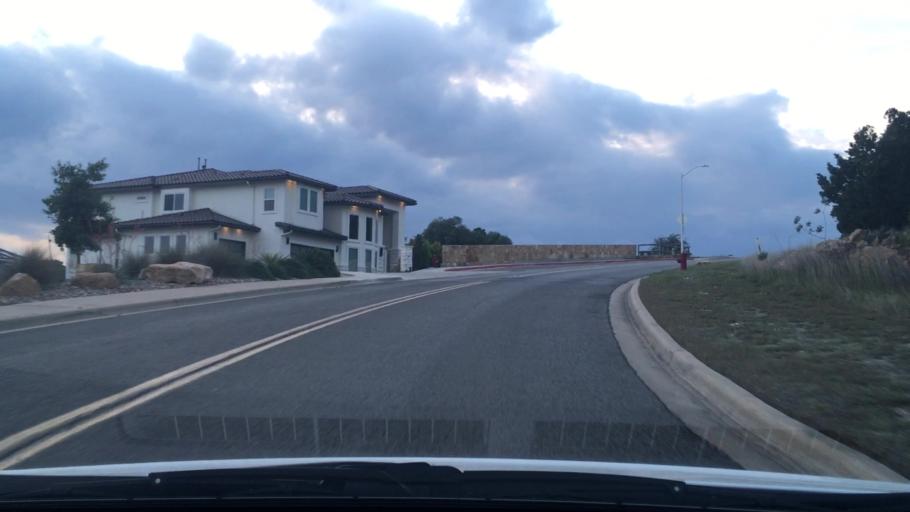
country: US
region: Texas
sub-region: Williamson County
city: Anderson Mill
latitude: 30.4515
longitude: -97.8582
